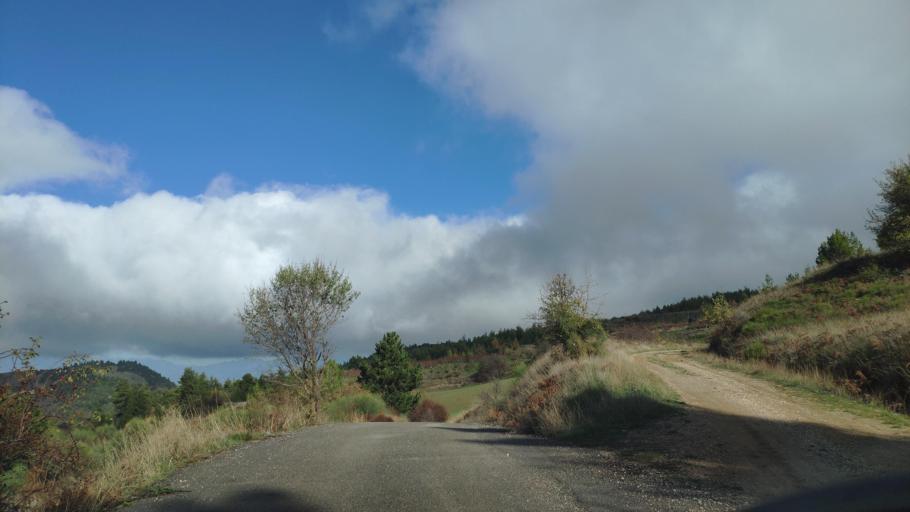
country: GR
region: West Greece
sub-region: Nomos Achaias
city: Aiyira
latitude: 38.0710
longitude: 22.4680
